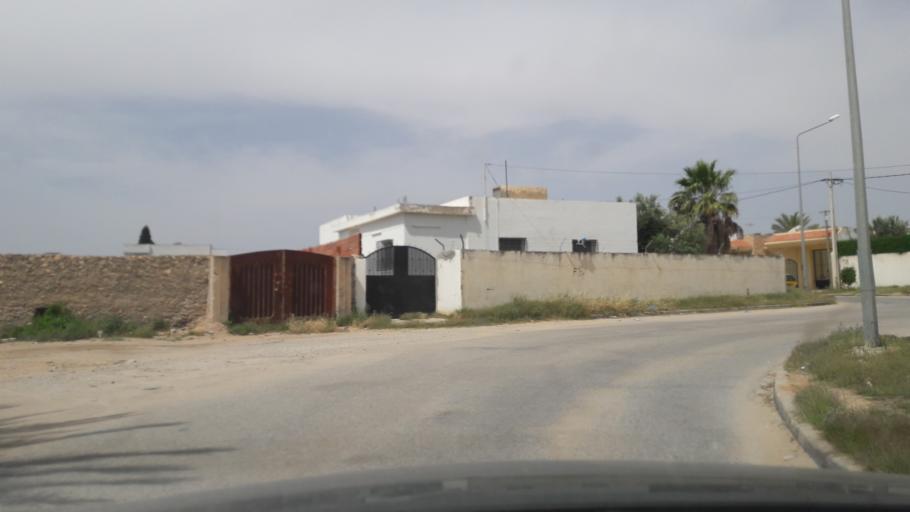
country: TN
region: Safaqis
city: Al Qarmadah
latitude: 34.7849
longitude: 10.7558
